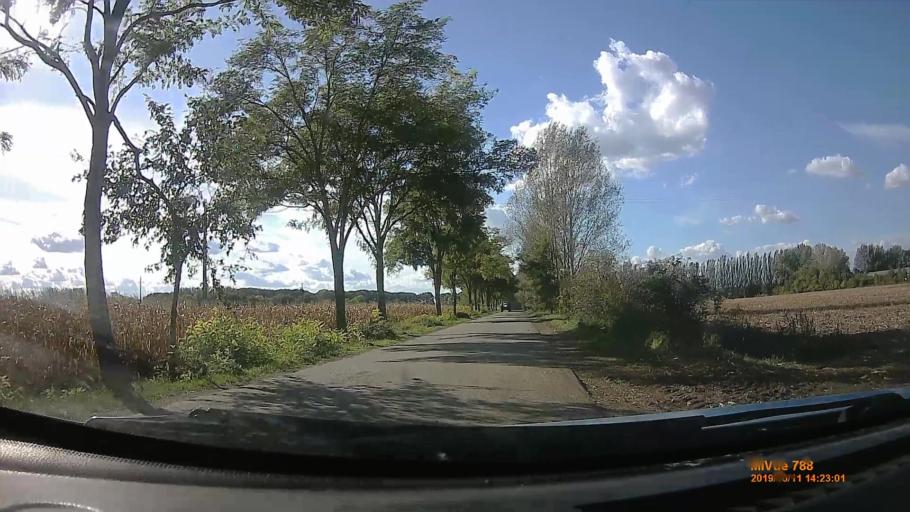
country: HU
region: Hajdu-Bihar
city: Hajduszoboszlo
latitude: 47.5288
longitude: 21.3620
